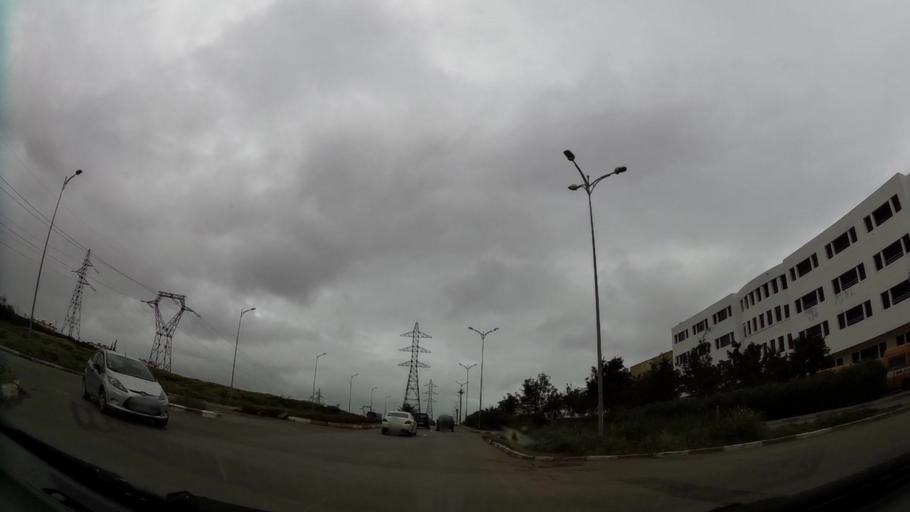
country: MA
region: Grand Casablanca
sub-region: Casablanca
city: Casablanca
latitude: 33.5289
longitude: -7.6170
